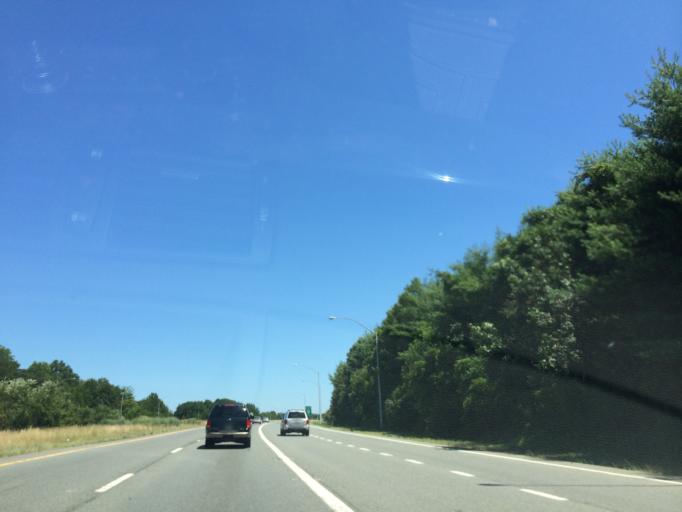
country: US
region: Maryland
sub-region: Howard County
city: Riverside
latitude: 39.1833
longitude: -76.8824
